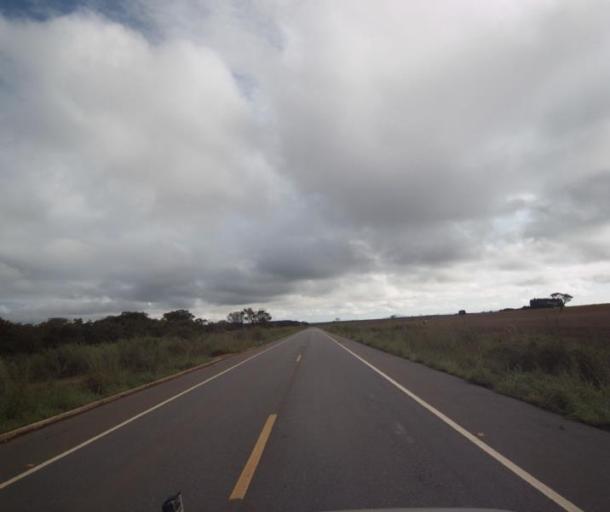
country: BR
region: Goias
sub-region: Padre Bernardo
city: Padre Bernardo
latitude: -15.3424
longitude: -48.6474
